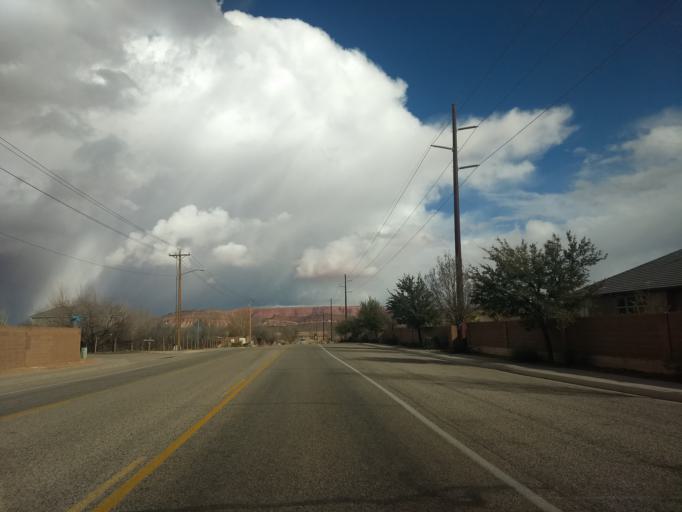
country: US
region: Utah
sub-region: Washington County
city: Saint George
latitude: 37.0668
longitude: -113.5350
